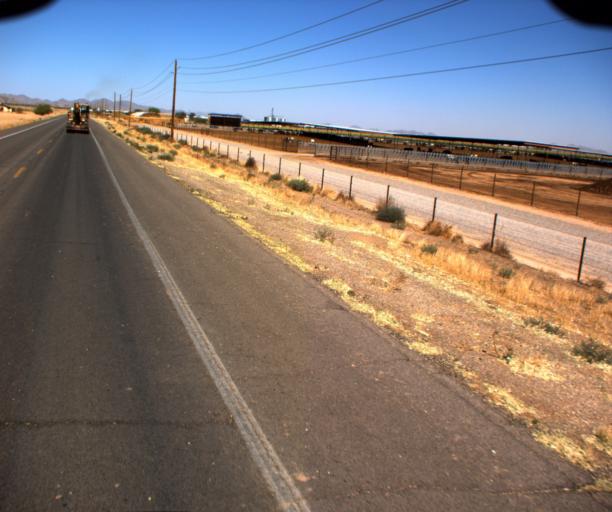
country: US
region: Arizona
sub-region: Pinal County
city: Maricopa
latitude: 32.8794
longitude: -112.0003
